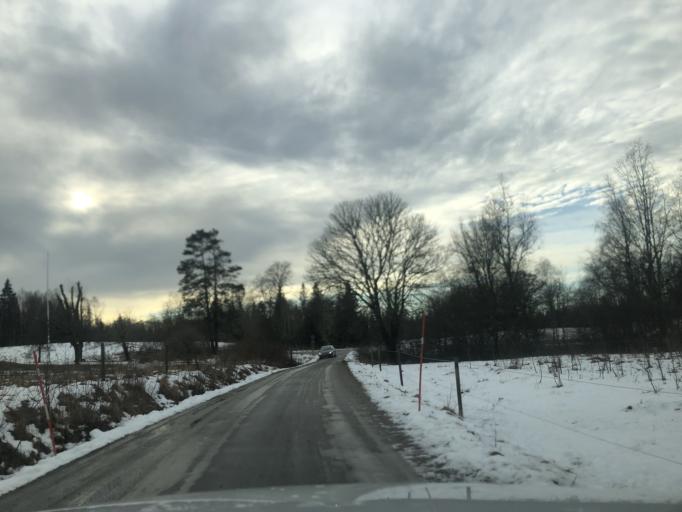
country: SE
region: Vaestra Goetaland
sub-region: Ulricehamns Kommun
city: Ulricehamn
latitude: 57.7675
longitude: 13.4671
